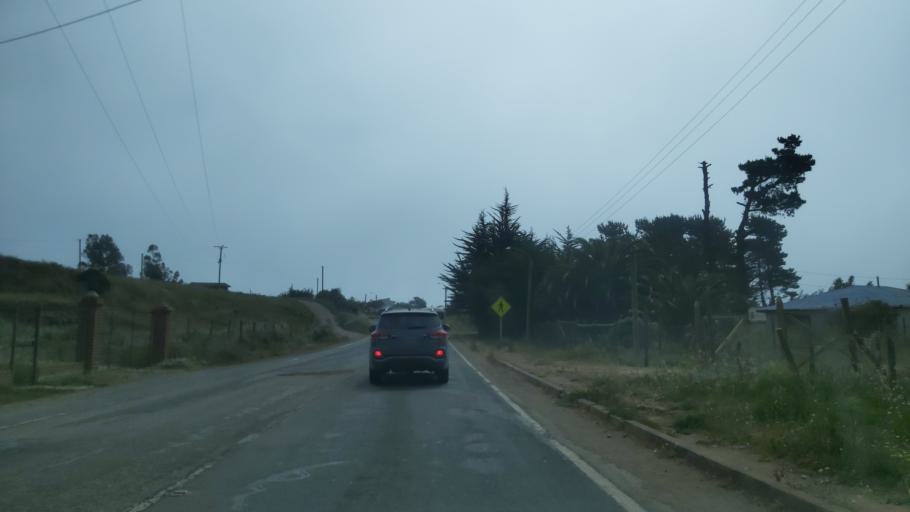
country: CL
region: Maule
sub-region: Provincia de Cauquenes
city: Cauquenes
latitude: -35.8742
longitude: -72.6644
